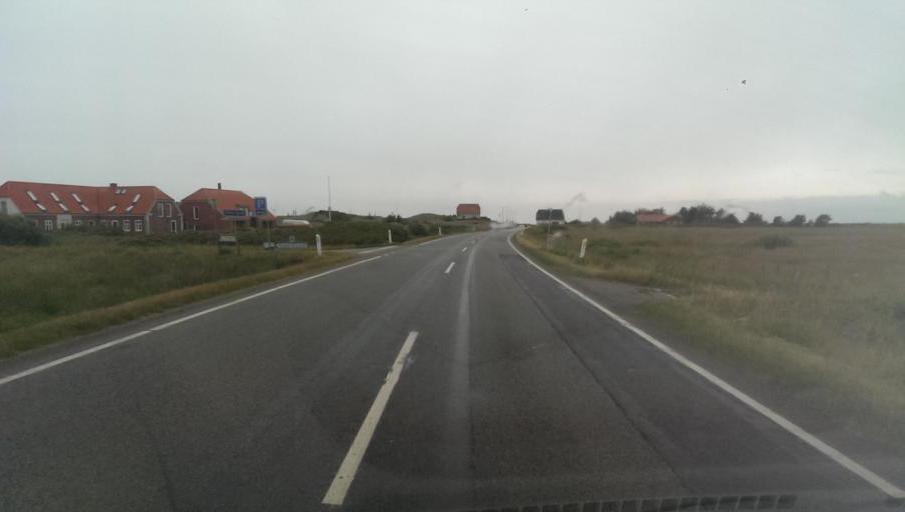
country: DK
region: Central Jutland
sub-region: Ringkobing-Skjern Kommune
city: Hvide Sande
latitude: 55.9767
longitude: 8.1406
